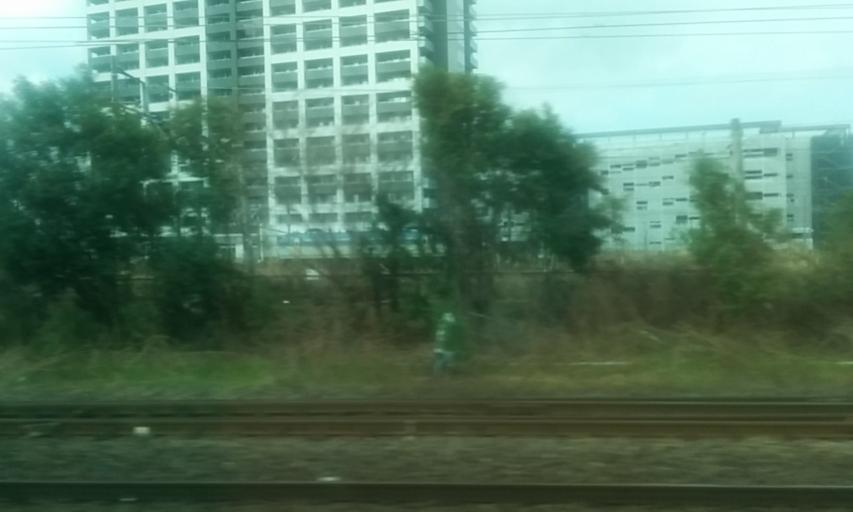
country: JP
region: Kanagawa
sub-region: Kawasaki-shi
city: Kawasaki
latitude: 35.5531
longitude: 139.6711
